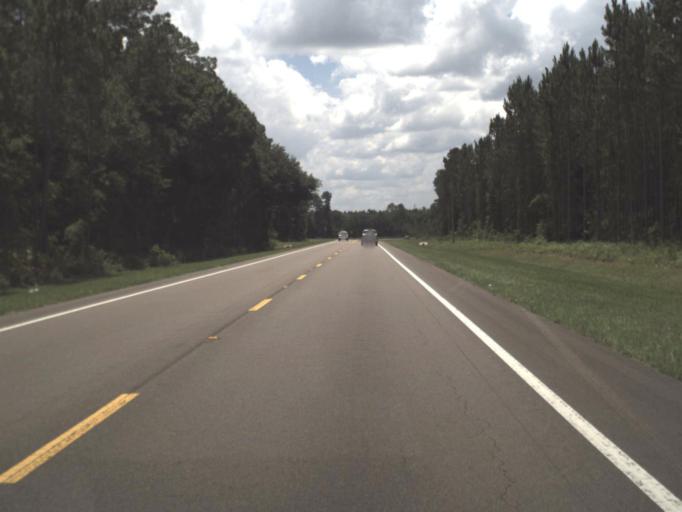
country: US
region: Florida
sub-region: Alachua County
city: Alachua
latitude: 29.7605
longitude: -82.3597
